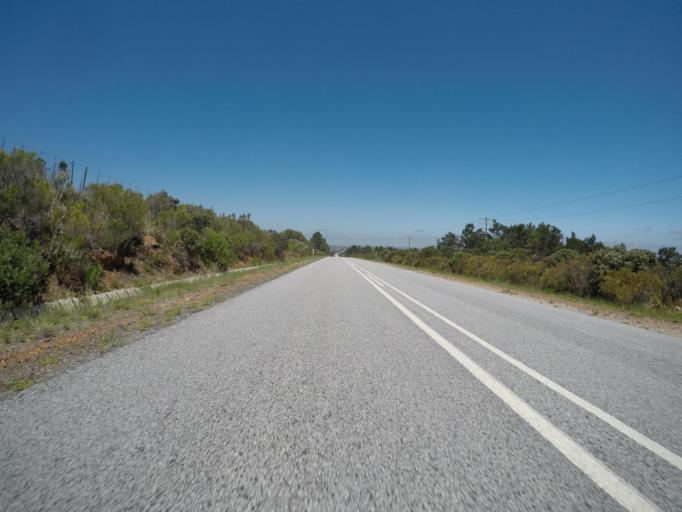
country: ZA
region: Eastern Cape
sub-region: Cacadu District Municipality
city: Kruisfontein
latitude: -33.9950
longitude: 24.5368
